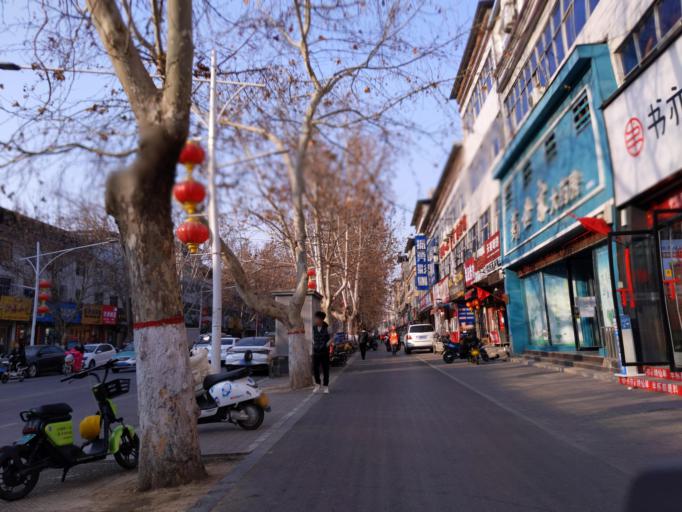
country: CN
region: Henan Sheng
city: Puyang
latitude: 35.7697
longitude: 115.0326
